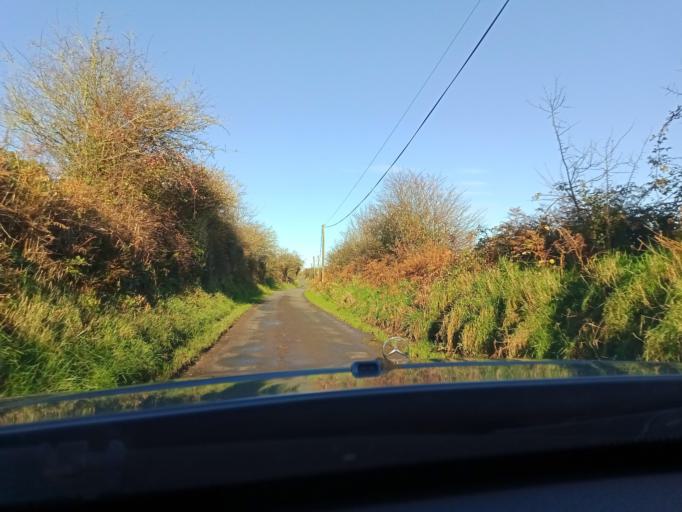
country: IE
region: Leinster
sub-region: Kilkenny
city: Mooncoin
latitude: 52.2945
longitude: -7.2082
